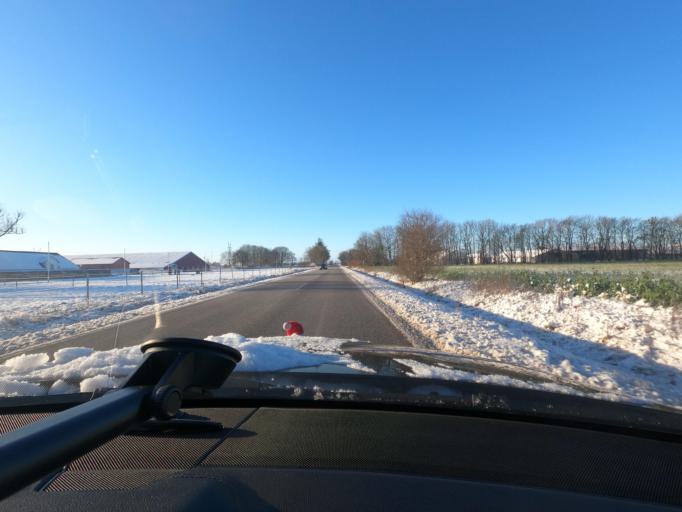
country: DK
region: South Denmark
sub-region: Aabenraa Kommune
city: Rodekro
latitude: 55.0747
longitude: 9.2766
